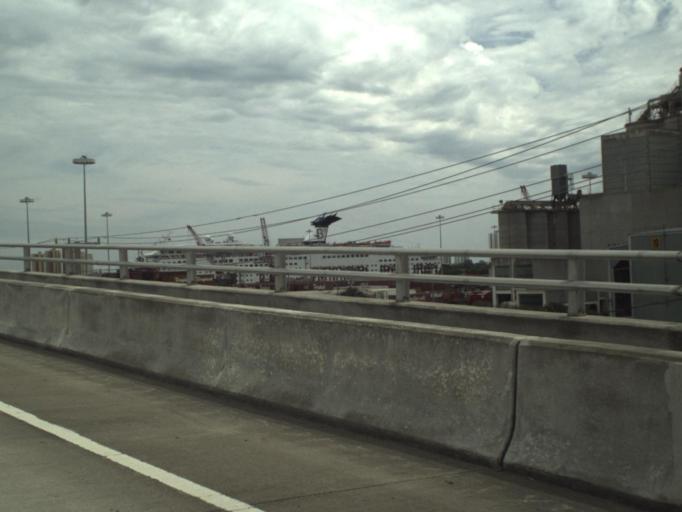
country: US
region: Florida
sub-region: Palm Beach County
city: Riviera Beach
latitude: 26.7656
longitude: -80.0552
